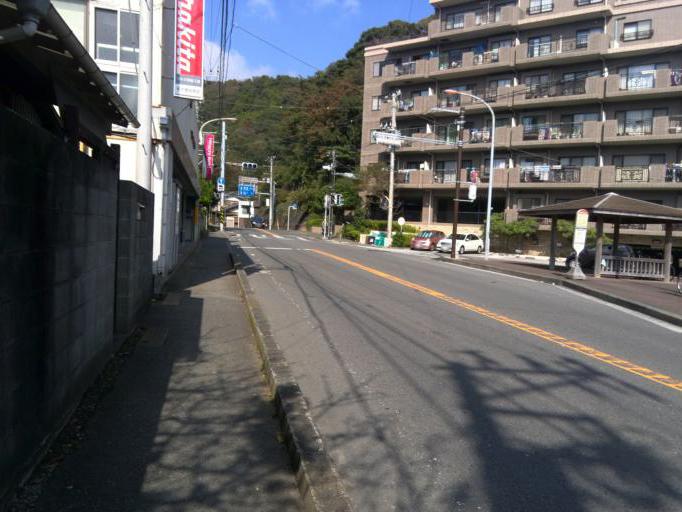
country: JP
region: Kanagawa
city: Hayama
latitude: 35.2836
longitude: 139.5802
